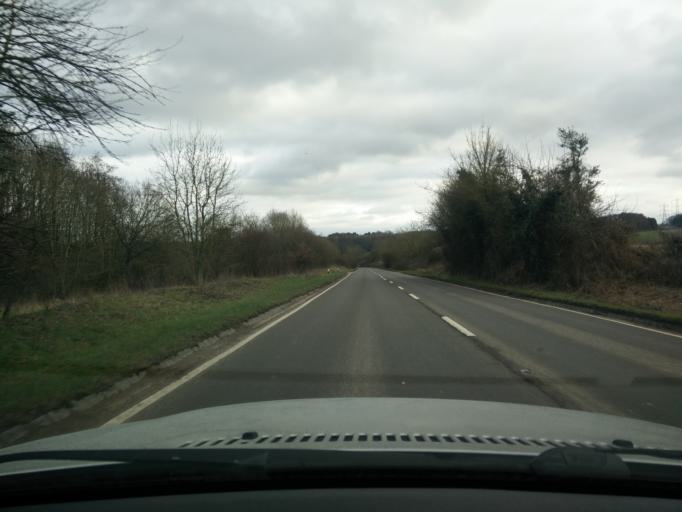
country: GB
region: England
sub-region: Buckinghamshire
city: Amersham
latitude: 51.6553
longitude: -0.6516
